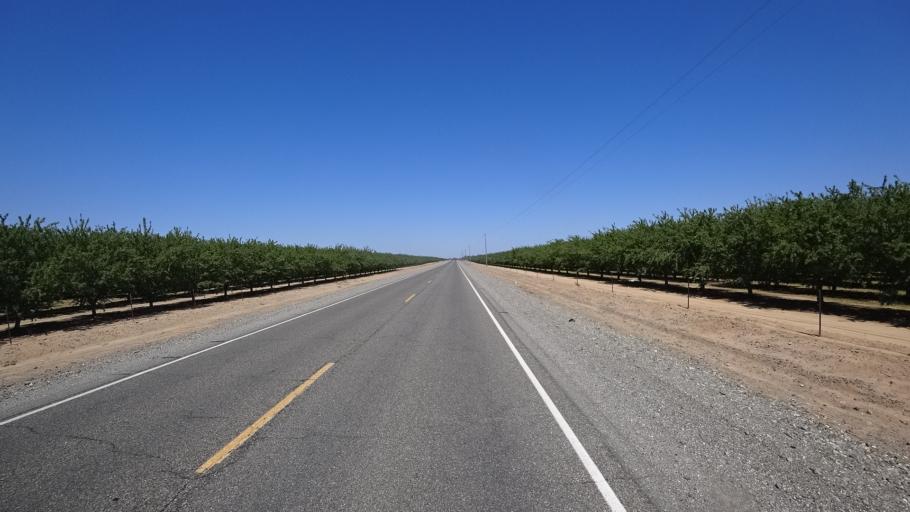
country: US
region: California
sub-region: Glenn County
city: Orland
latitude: 39.6710
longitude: -122.1970
